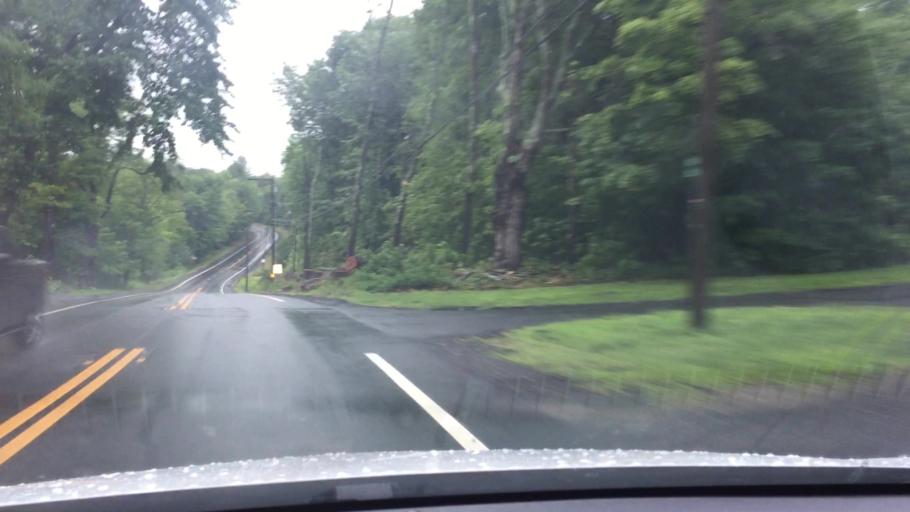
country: US
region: Massachusetts
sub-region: Berkshire County
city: Becket
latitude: 42.3055
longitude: -73.0647
